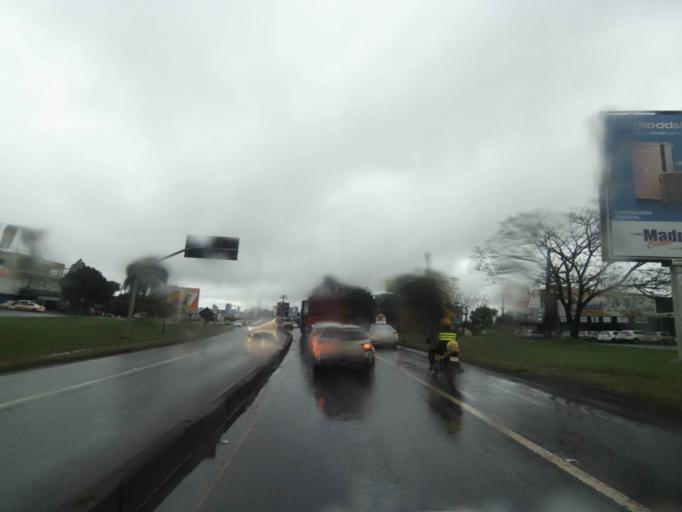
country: PY
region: Alto Parana
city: Ciudad del Este
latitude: -25.5060
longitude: -54.5892
